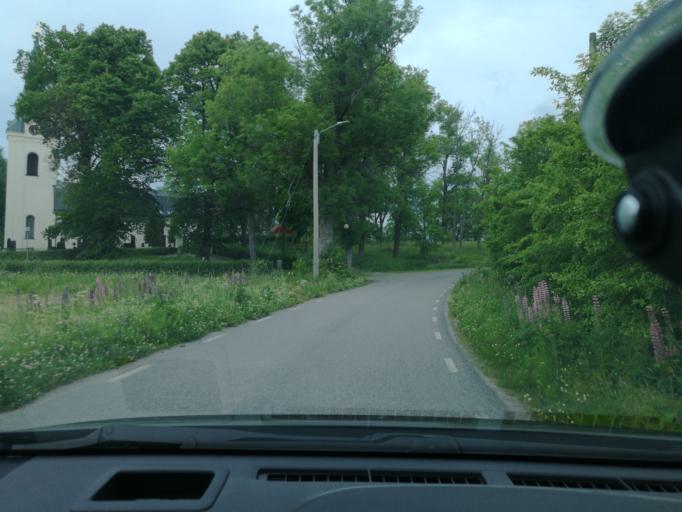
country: SE
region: Vaestmanland
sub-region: Vasteras
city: Skultuna
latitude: 59.8738
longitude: 16.3439
